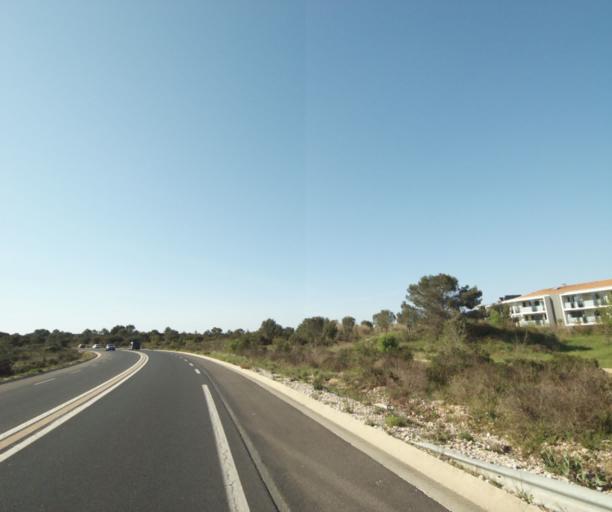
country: FR
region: Languedoc-Roussillon
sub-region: Departement de l'Herault
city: Le Cres
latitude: 43.6502
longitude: 3.9273
